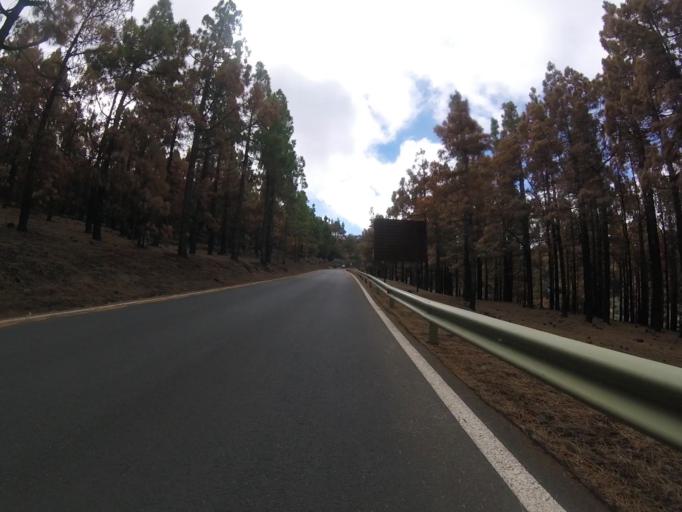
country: ES
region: Canary Islands
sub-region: Provincia de Las Palmas
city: San Bartolome
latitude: 27.9681
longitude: -15.5652
